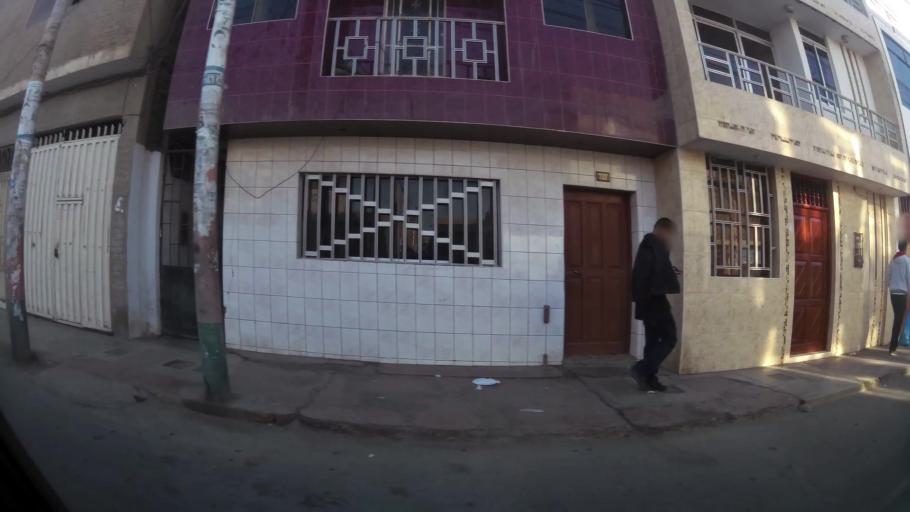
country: PE
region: Lima
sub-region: Huaura
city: Huacho
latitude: -11.1120
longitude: -77.6055
